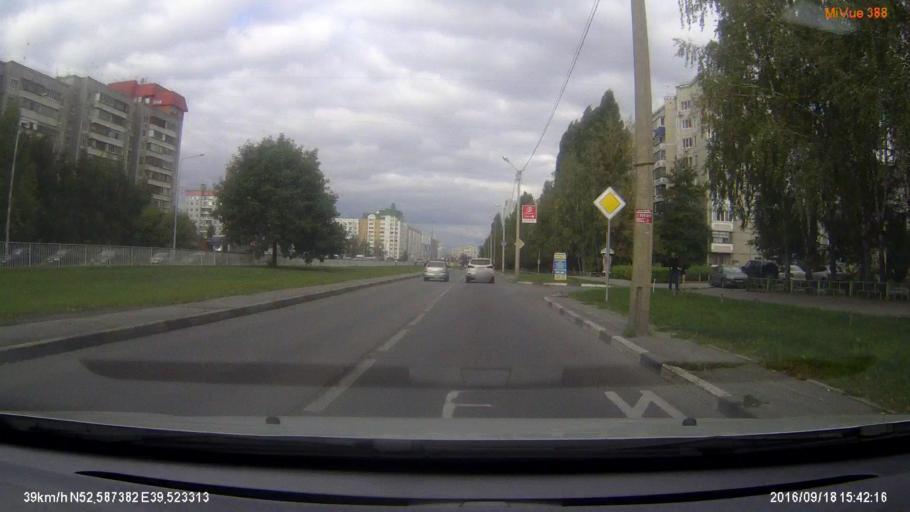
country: RU
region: Lipetsk
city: Syrskoye
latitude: 52.5875
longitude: 39.5237
